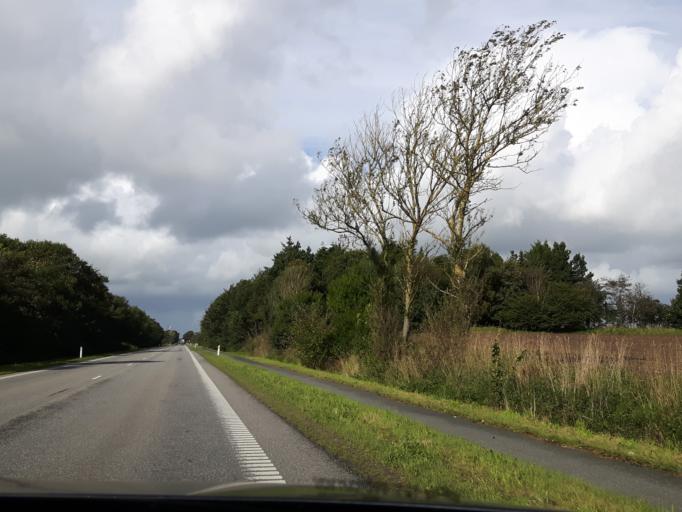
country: DK
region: North Denmark
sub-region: Morso Kommune
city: Nykobing Mors
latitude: 57.0309
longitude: 8.9872
